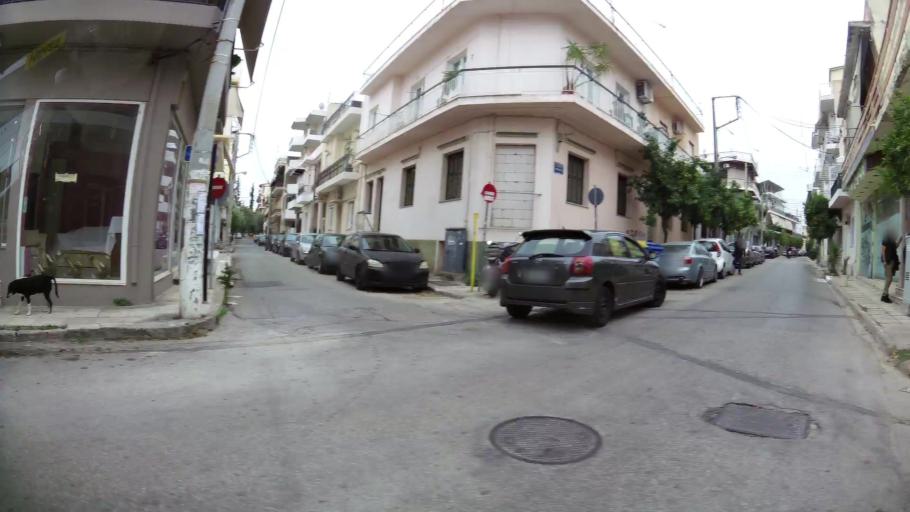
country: GR
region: Attica
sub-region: Nomarchia Athinas
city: Aigaleo
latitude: 38.0005
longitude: 23.6822
